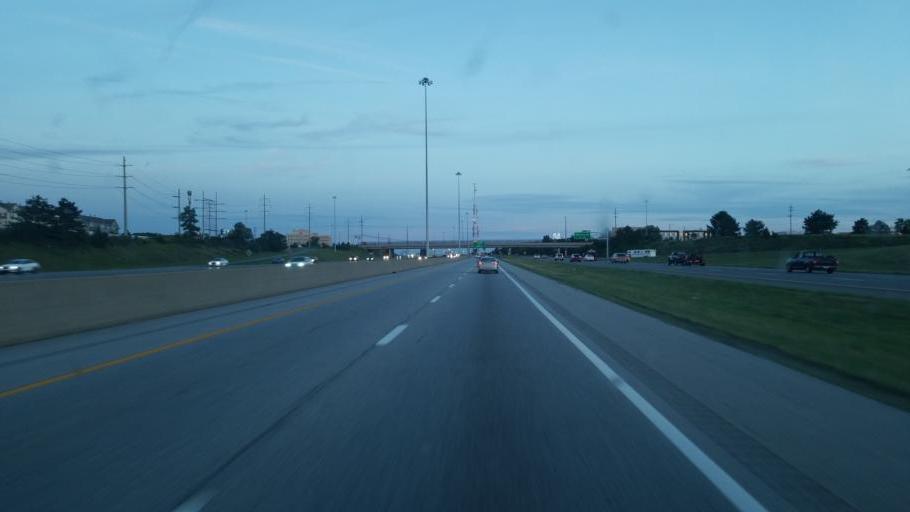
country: US
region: Ohio
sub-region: Cuyahoga County
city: Beachwood
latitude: 41.4673
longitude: -81.4899
